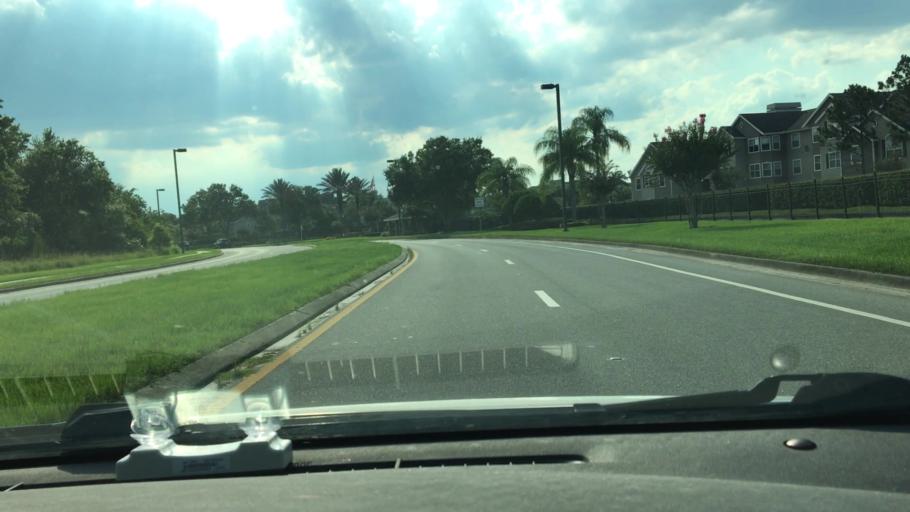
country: US
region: Florida
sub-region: Orange County
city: Conway
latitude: 28.4727
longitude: -81.2984
